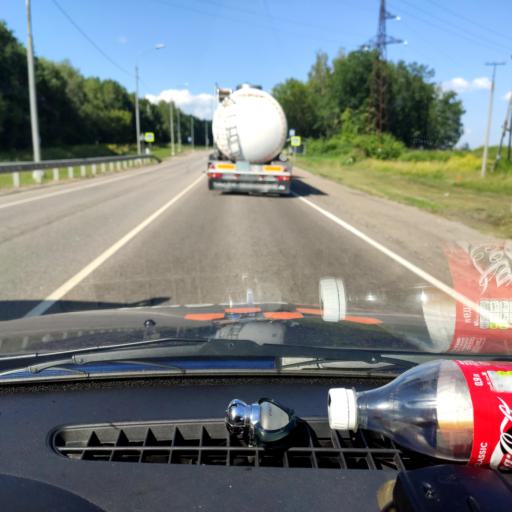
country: RU
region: Lipetsk
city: Kazaki
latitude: 52.5976
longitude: 38.2425
